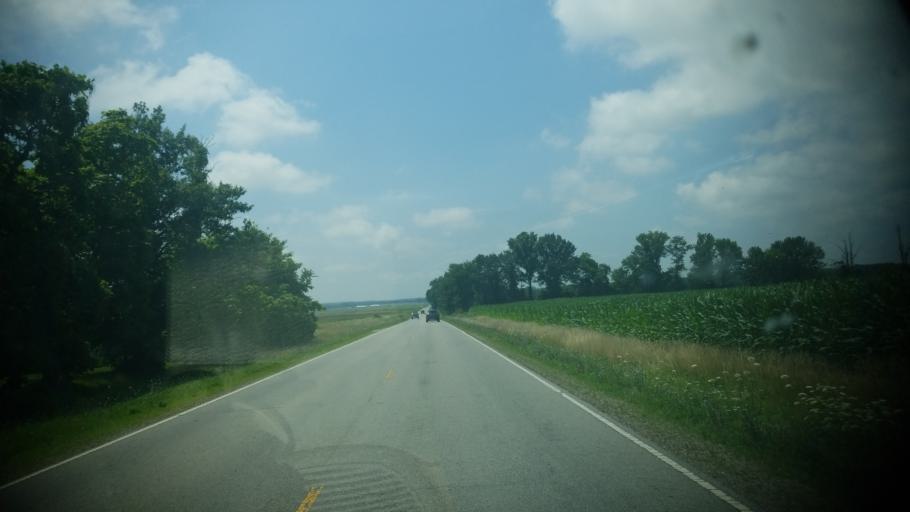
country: US
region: Illinois
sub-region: Wayne County
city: Fairfield
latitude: 38.4680
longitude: -88.3490
